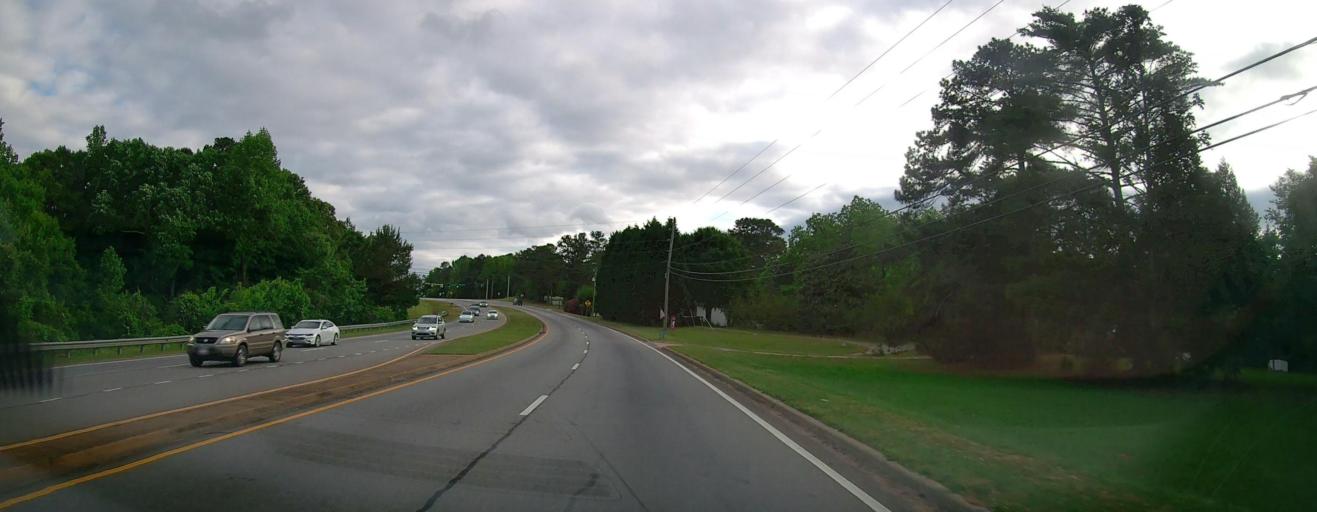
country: US
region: Georgia
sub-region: Oconee County
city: Watkinsville
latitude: 33.9015
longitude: -83.4080
